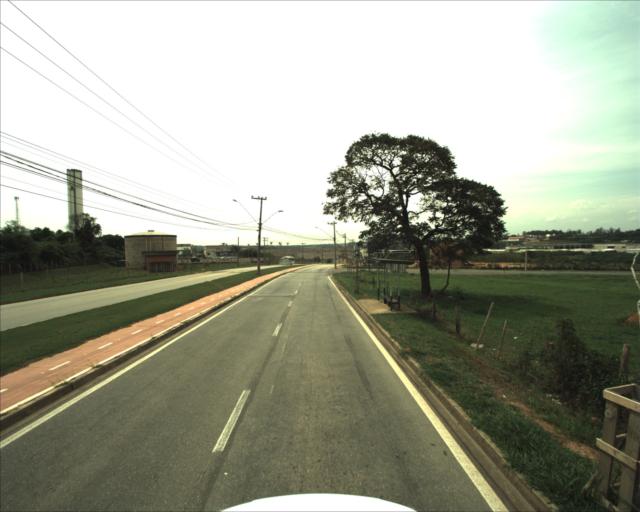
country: BR
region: Sao Paulo
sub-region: Sorocaba
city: Sorocaba
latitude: -23.4357
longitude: -47.4369
